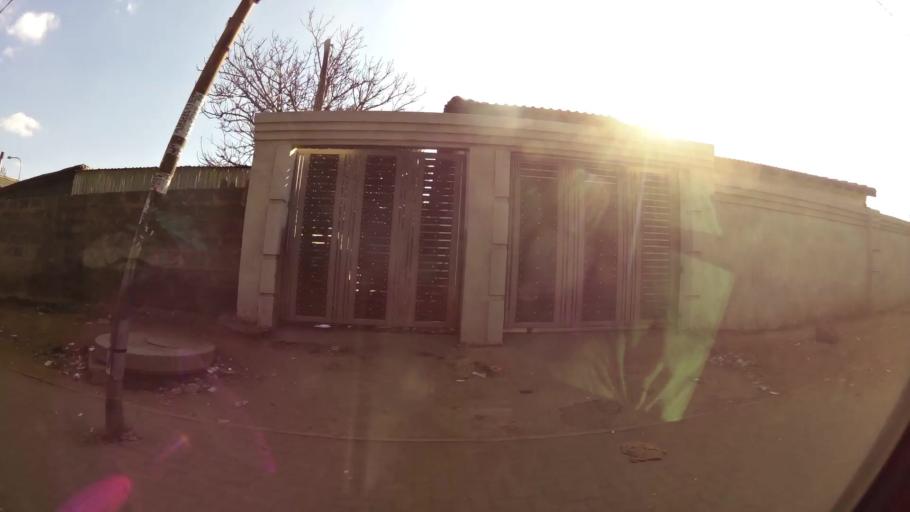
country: ZA
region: Gauteng
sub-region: City of Johannesburg Metropolitan Municipality
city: Soweto
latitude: -26.2215
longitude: 27.8739
